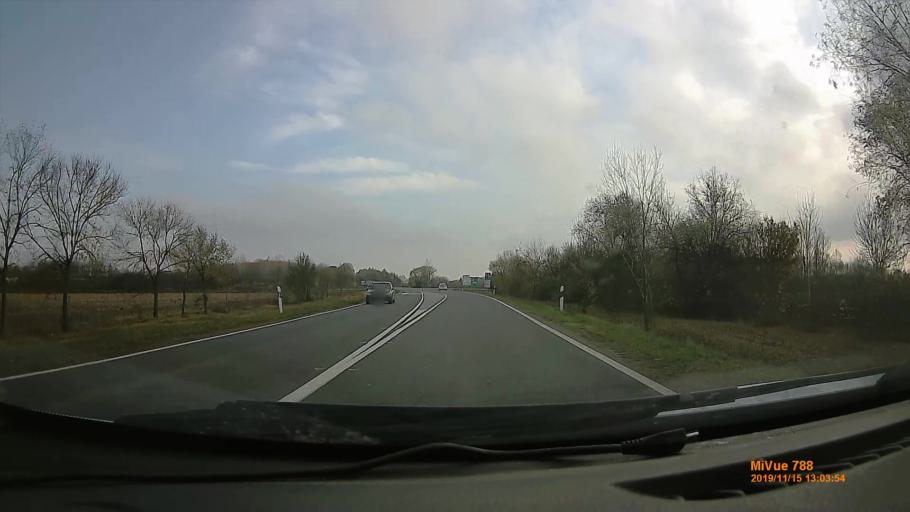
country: HU
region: Bekes
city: Gyula
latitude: 46.6389
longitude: 21.2481
